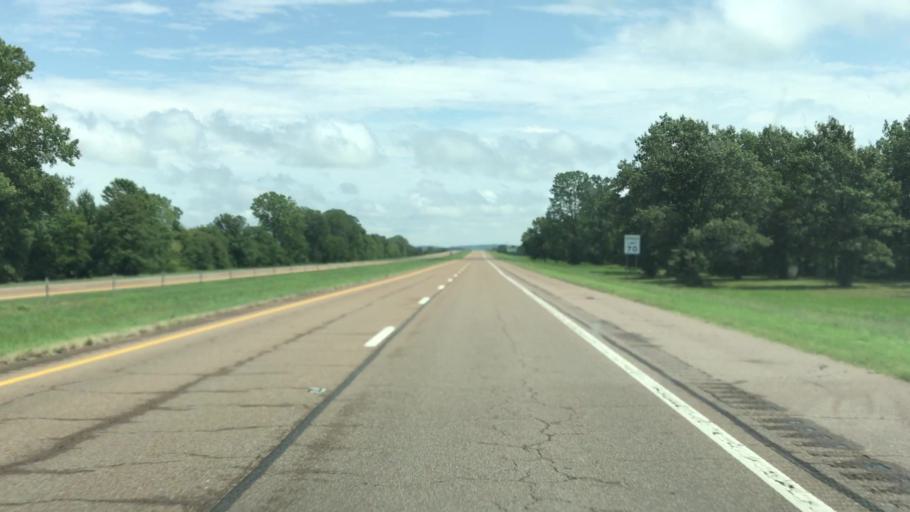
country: US
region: Missouri
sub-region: Pemiscot County
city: Caruthersville
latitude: 36.0914
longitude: -89.5784
